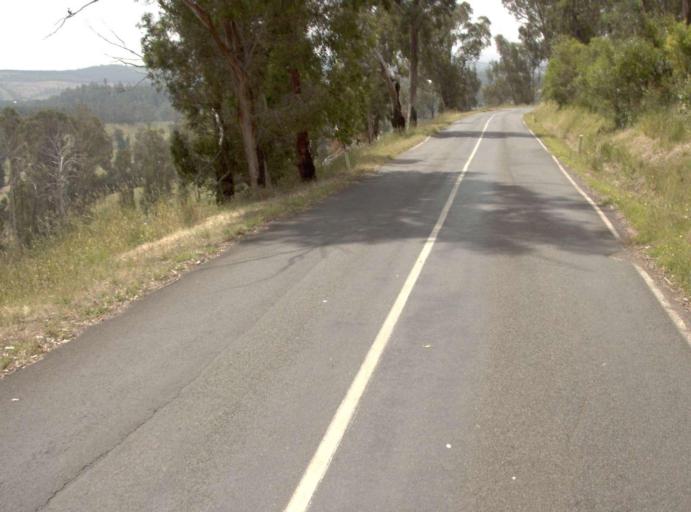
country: AU
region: Victoria
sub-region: Latrobe
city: Traralgon
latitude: -38.3240
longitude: 146.5706
